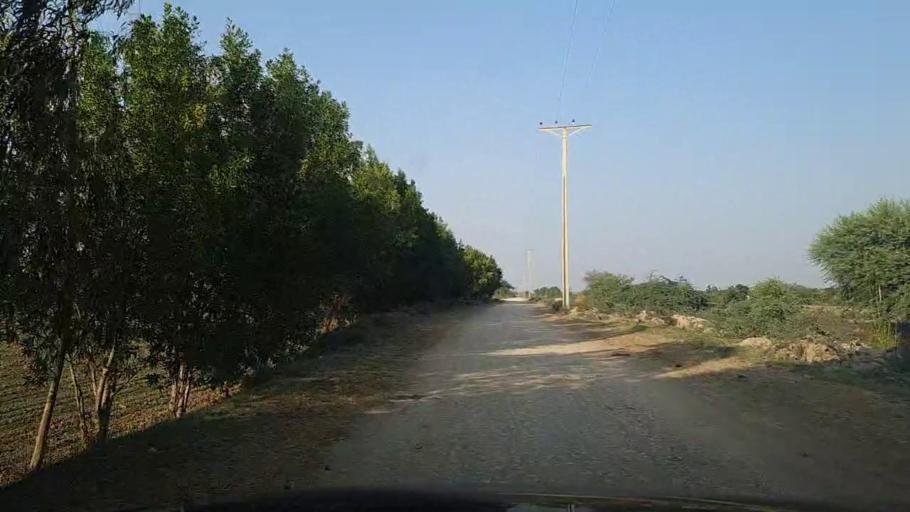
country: PK
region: Sindh
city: Thatta
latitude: 24.7478
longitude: 67.9580
